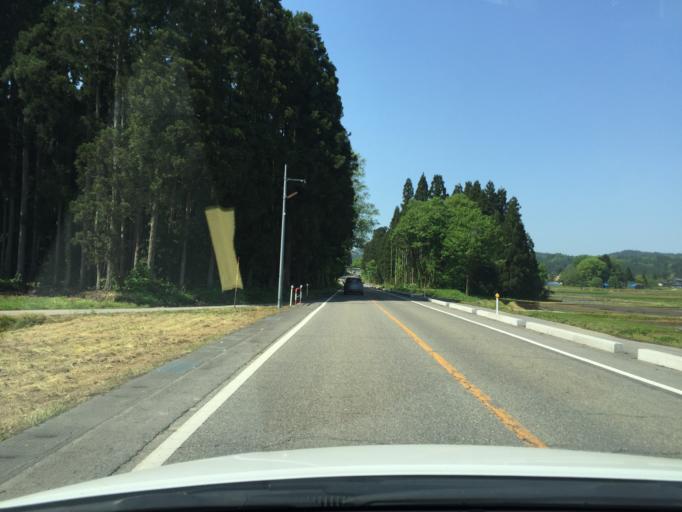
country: JP
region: Niigata
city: Muramatsu
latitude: 37.6687
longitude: 139.1442
